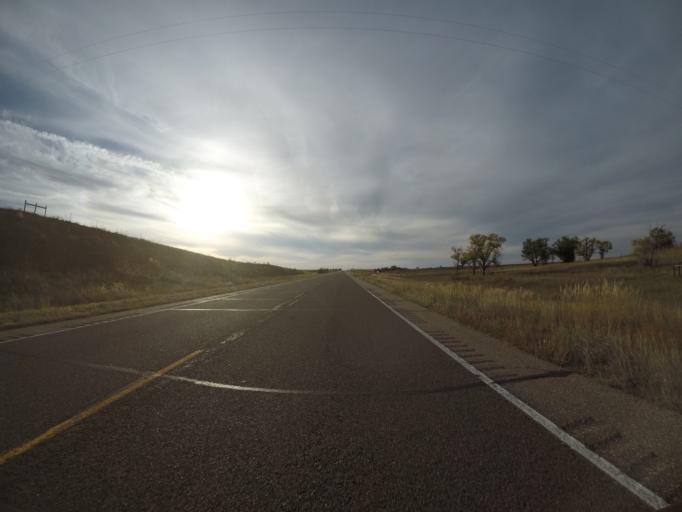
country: US
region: Colorado
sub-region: Kit Carson County
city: Burlington
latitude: 39.6580
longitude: -102.5132
